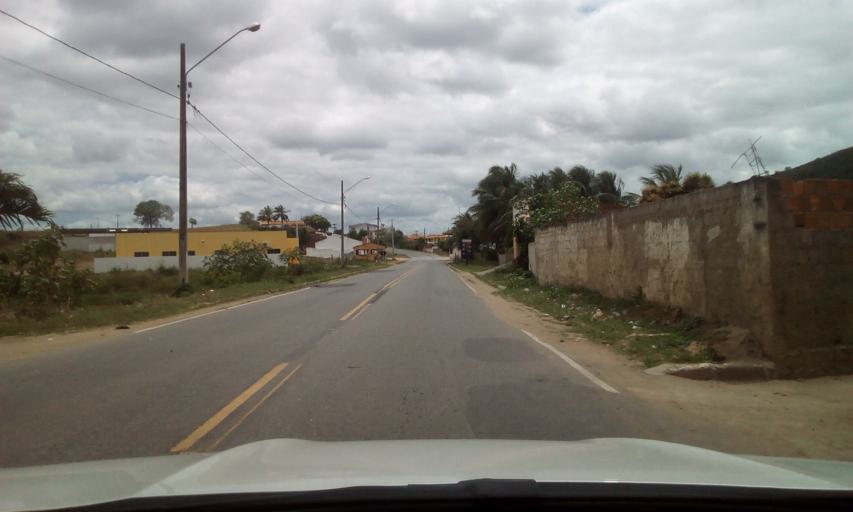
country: BR
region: Paraiba
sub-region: Serra Redonda
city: Alagoa Grande
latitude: -7.1699
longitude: -35.5918
